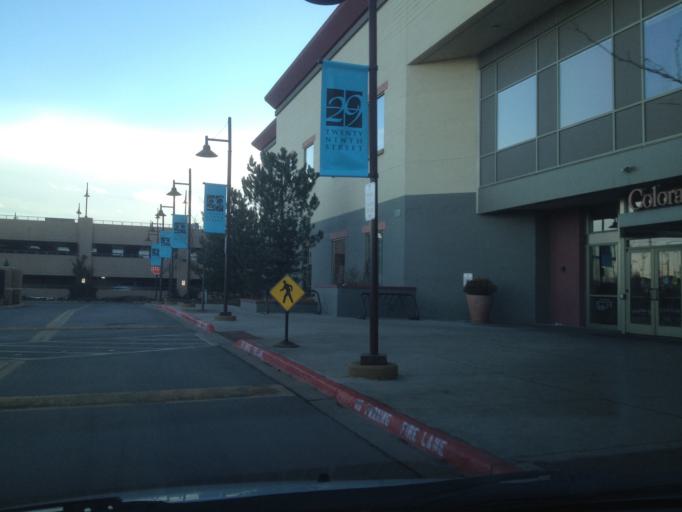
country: US
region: Colorado
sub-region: Boulder County
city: Boulder
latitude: 40.0190
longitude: -105.2544
